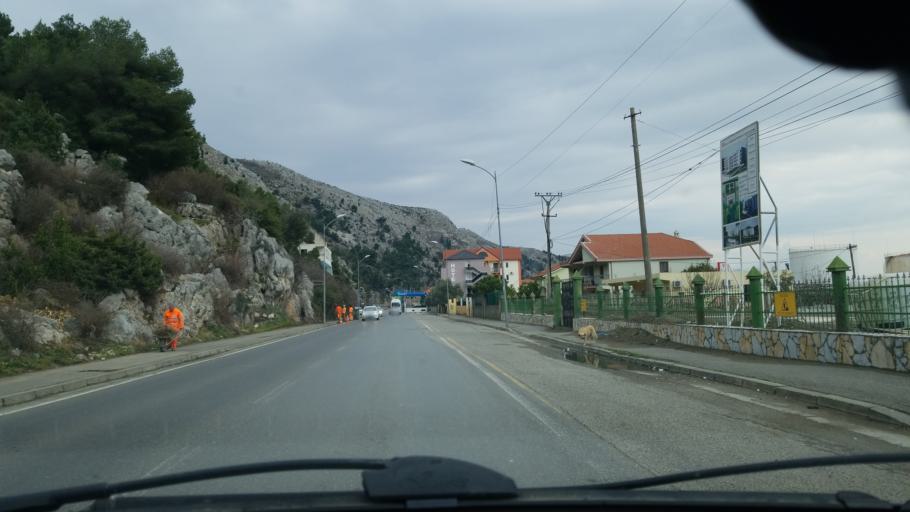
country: AL
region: Lezhe
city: Shengjin
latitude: 41.8075
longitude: 19.6066
